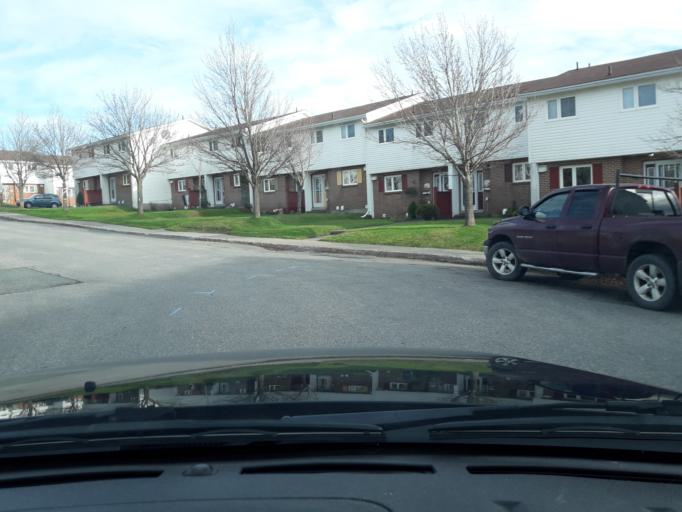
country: CA
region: Newfoundland and Labrador
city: St. John's
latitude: 47.5644
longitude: -52.7590
